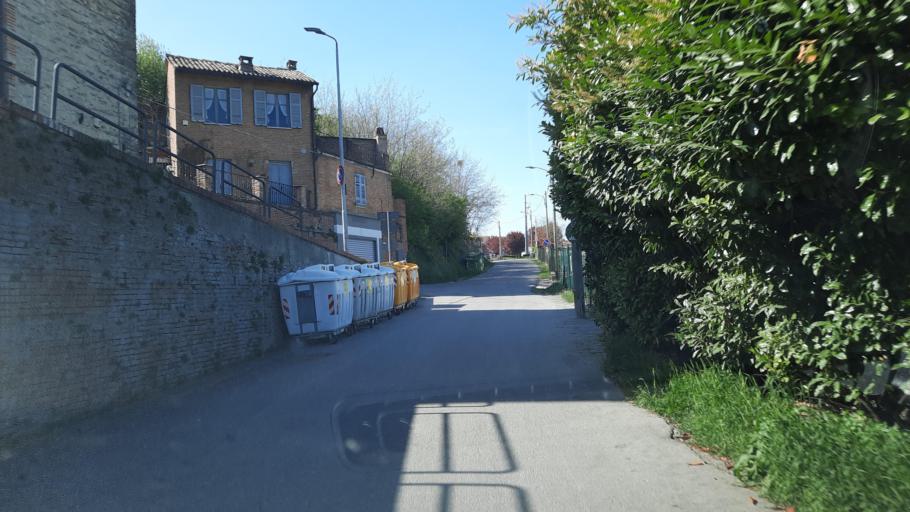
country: IT
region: Piedmont
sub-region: Provincia di Alessandria
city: Vignale Monferrato
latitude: 45.0105
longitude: 8.3999
